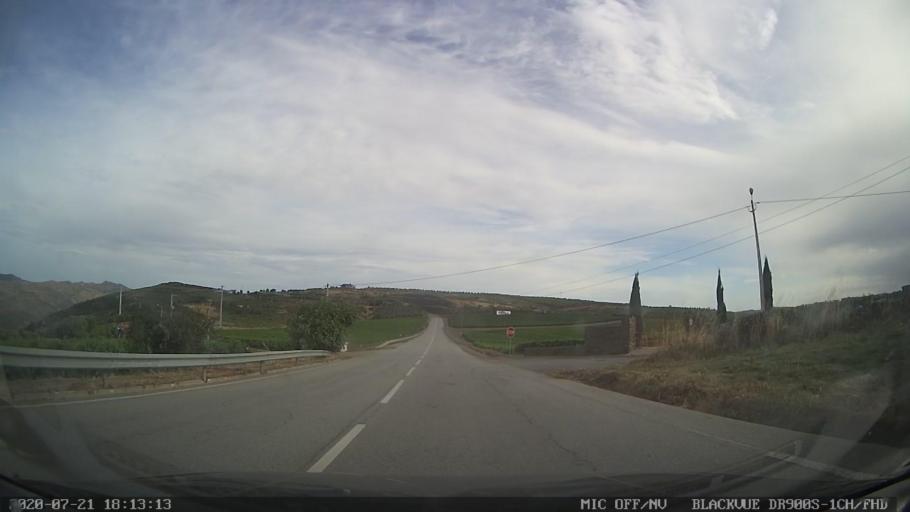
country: PT
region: Viseu
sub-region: Sao Joao da Pesqueira
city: Sao Joao da Pesqueira
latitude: 41.1327
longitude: -7.3984
